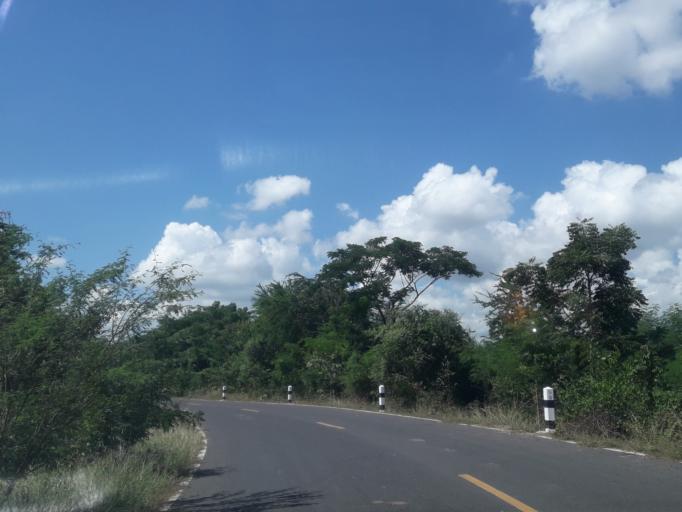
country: TH
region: Lop Buri
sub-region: Amphoe Tha Luang
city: Tha Luang
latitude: 15.0699
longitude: 101.0350
